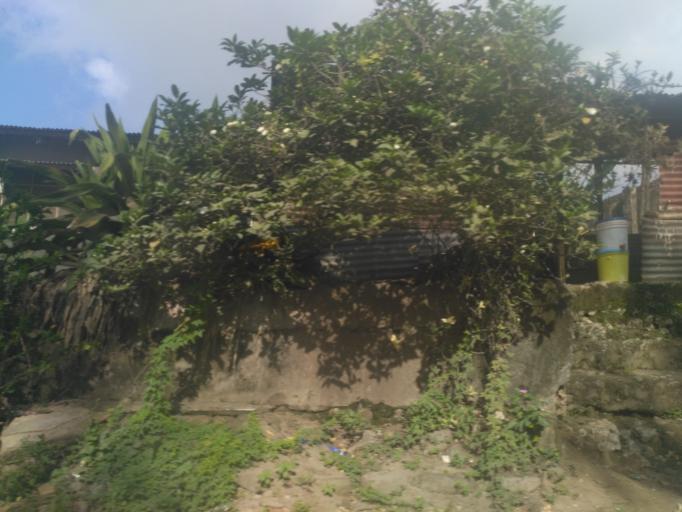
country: TZ
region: Zanzibar Urban/West
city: Zanzibar
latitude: -6.1703
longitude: 39.2248
